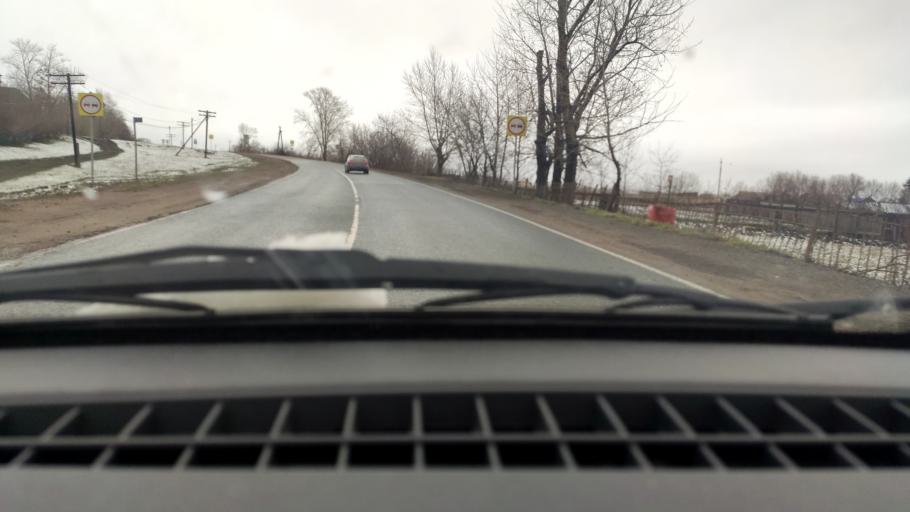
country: RU
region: Bashkortostan
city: Alekseyevka
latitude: 55.0518
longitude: 55.1282
